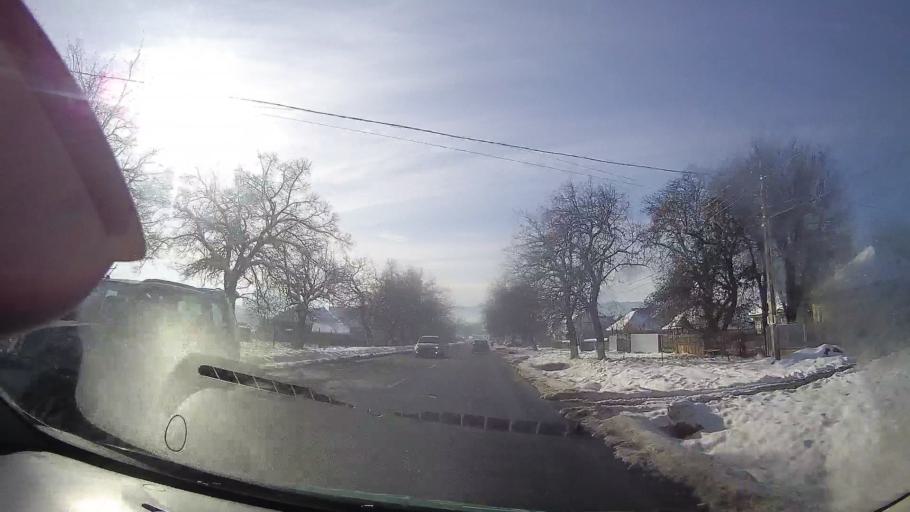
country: RO
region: Neamt
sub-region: Oras Targu Neamt
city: Humulesti
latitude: 47.1861
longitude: 26.3365
